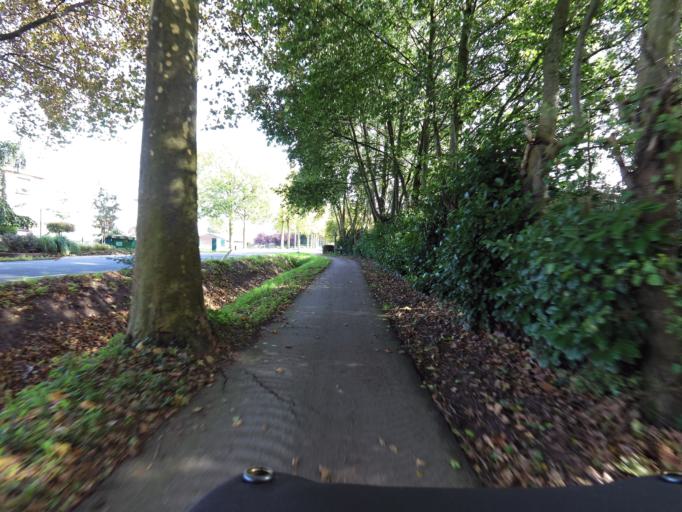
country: NL
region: Gelderland
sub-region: Gemeente Duiven
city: Duiven
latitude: 51.8902
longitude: 6.0114
